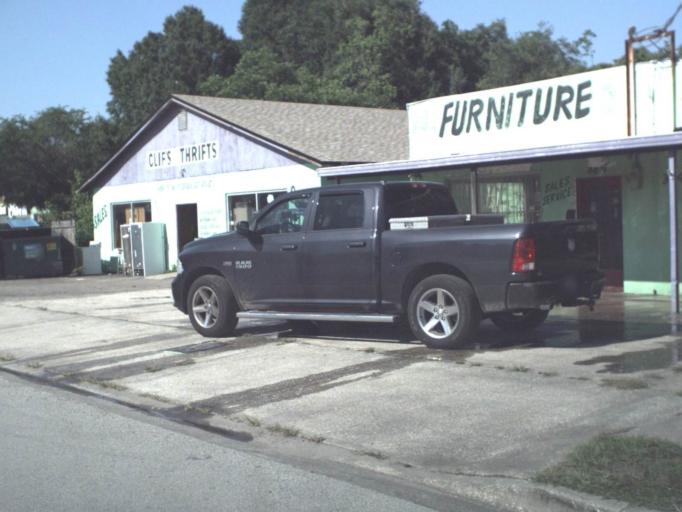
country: US
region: Florida
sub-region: Duval County
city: Jacksonville
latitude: 30.3346
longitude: -81.7310
